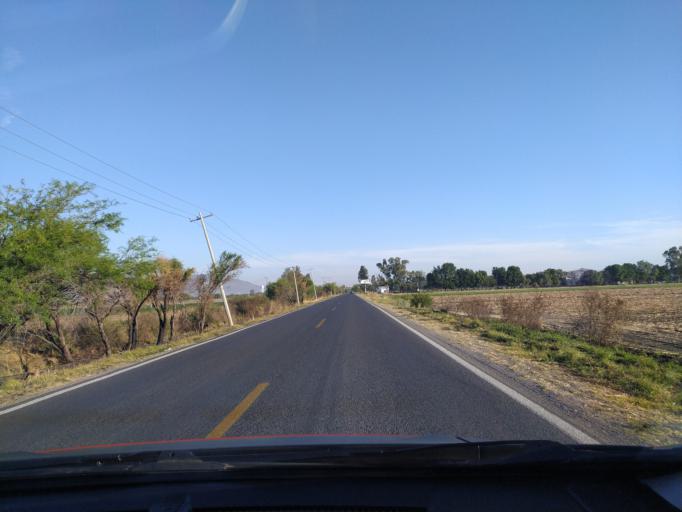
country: MX
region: Guanajuato
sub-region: San Francisco del Rincon
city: San Ignacio de Hidalgo
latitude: 20.9353
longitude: -101.8537
